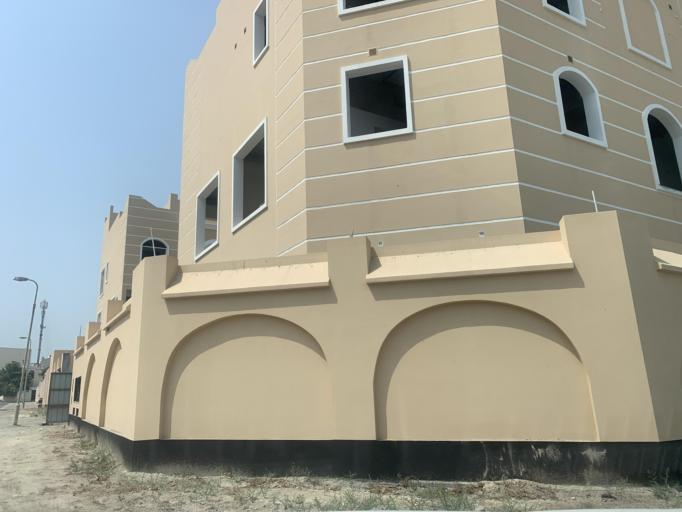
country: BH
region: Central Governorate
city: Madinat Hamad
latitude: 26.1630
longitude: 50.4537
